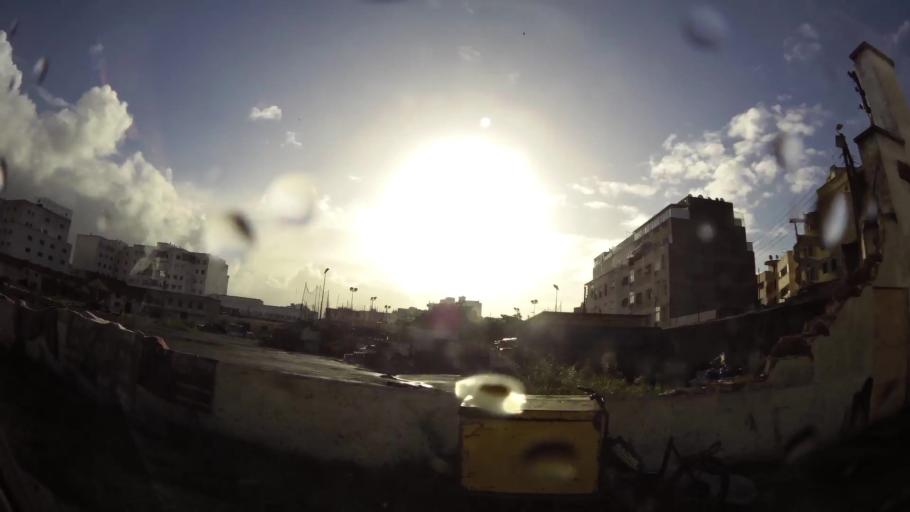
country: MA
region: Grand Casablanca
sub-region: Casablanca
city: Casablanca
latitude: 33.5889
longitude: -7.6004
